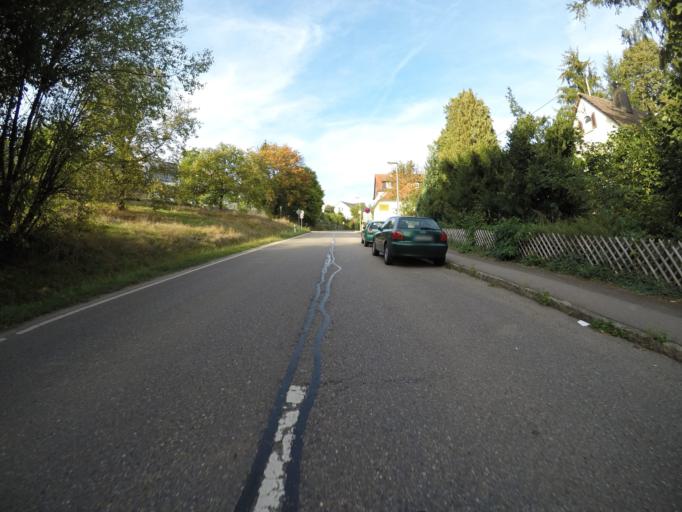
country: DE
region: Baden-Wuerttemberg
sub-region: Regierungsbezirk Stuttgart
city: Neuhausen auf den Fildern
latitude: 48.7065
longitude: 9.2900
